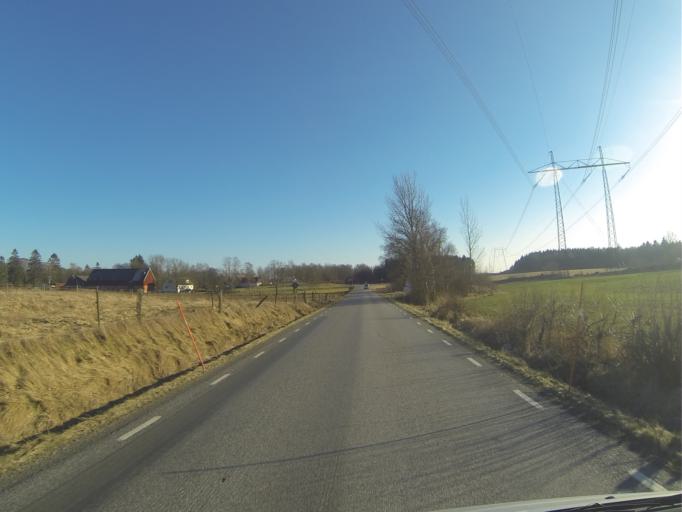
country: SE
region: Skane
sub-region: Horby Kommun
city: Hoerby
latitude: 55.8794
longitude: 13.6640
